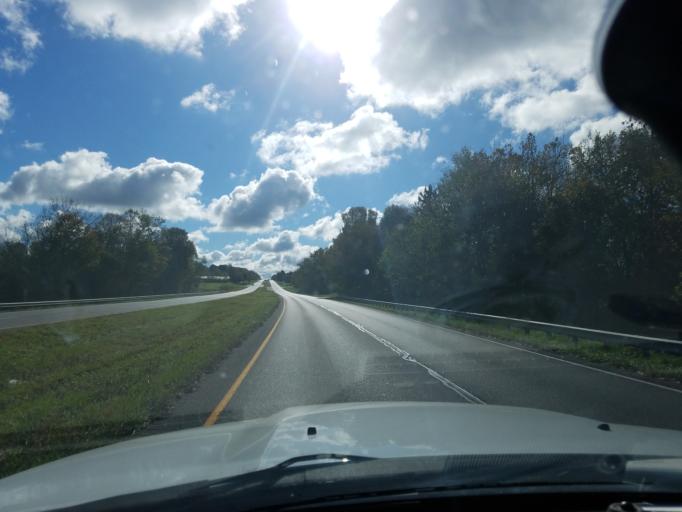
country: US
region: Kentucky
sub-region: Lincoln County
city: Stanford
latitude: 37.5717
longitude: -84.6980
